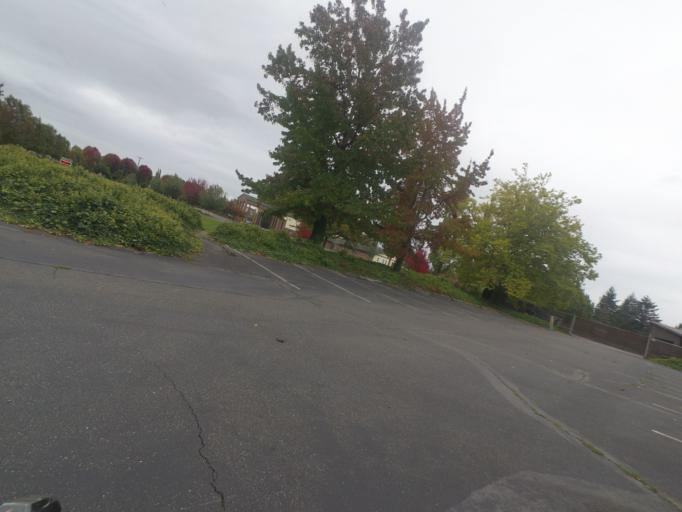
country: US
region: Washington
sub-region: Pierce County
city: Lakewood
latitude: 47.1556
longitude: -122.5101
